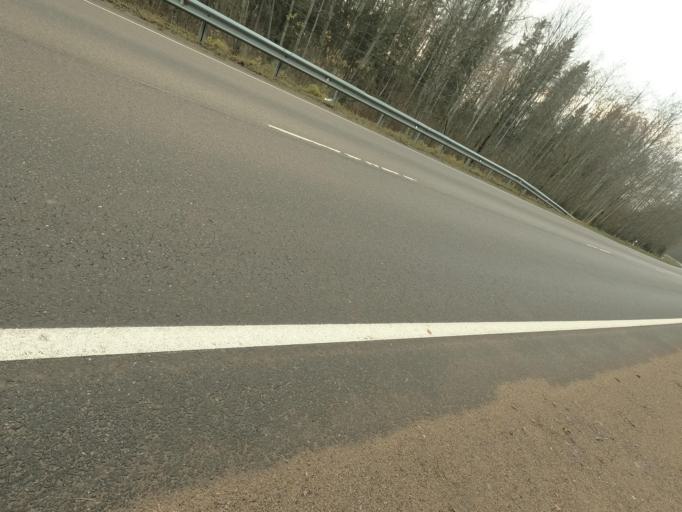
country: RU
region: Leningrad
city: Pavlovo
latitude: 59.8095
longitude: 30.9600
